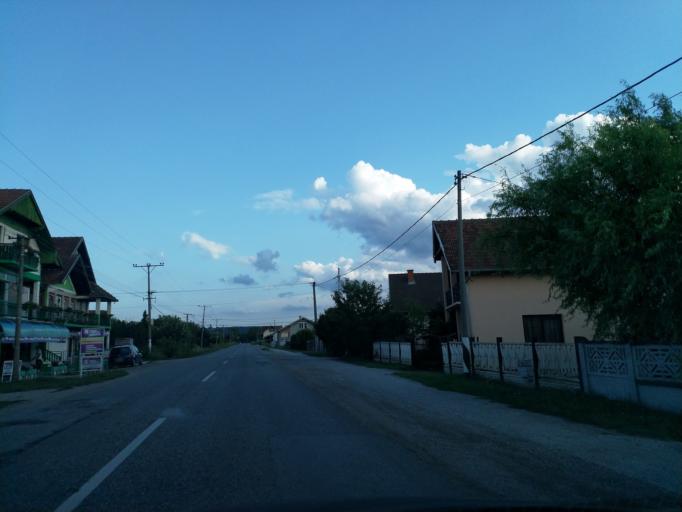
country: RS
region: Central Serbia
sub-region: Rasinski Okrug
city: Cicevac
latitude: 43.7608
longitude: 21.4317
